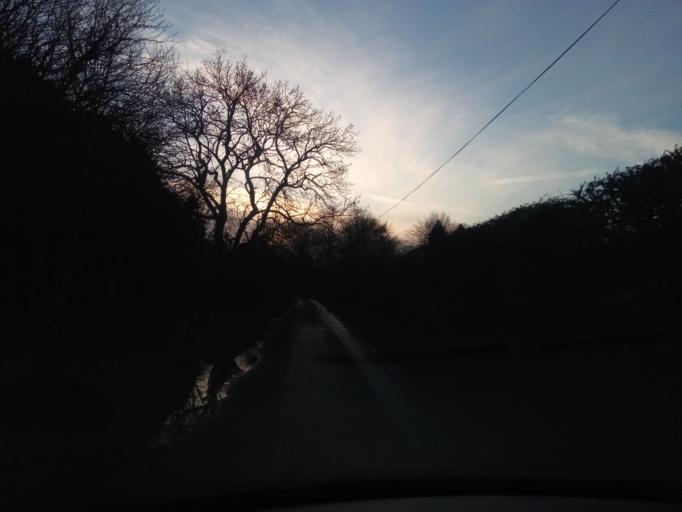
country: GB
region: Scotland
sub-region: The Scottish Borders
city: Saint Boswells
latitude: 55.5154
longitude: -2.6613
